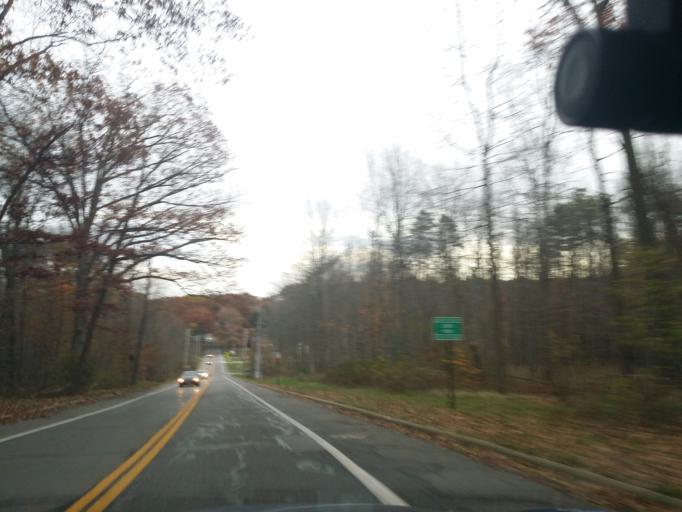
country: US
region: Ohio
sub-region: Cuyahoga County
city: North Olmsted
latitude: 41.4065
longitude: -81.8949
